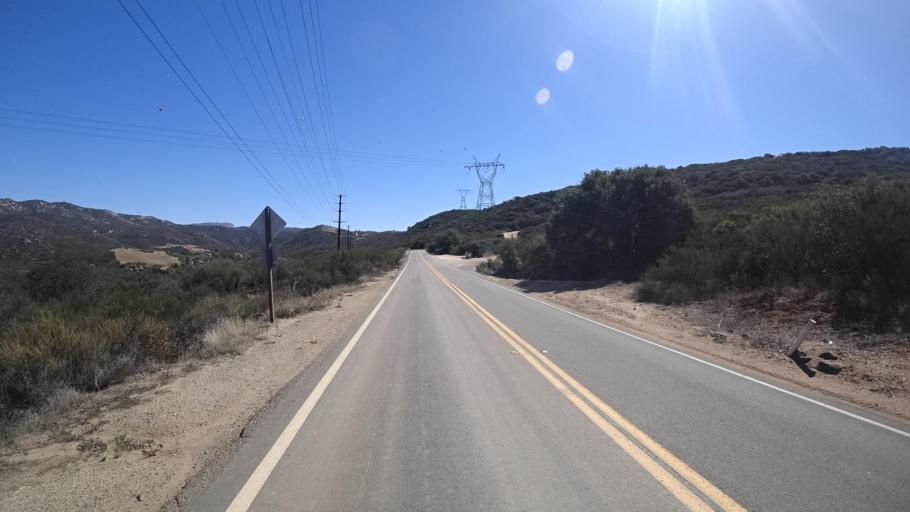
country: US
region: California
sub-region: San Diego County
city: Alpine
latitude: 32.7787
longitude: -116.7155
